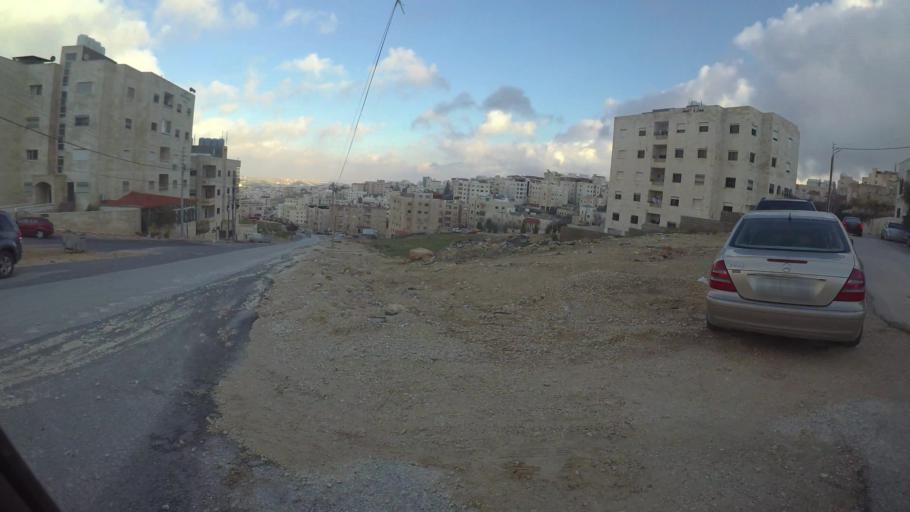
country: JO
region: Amman
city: Al Jubayhah
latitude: 32.0513
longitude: 35.8879
